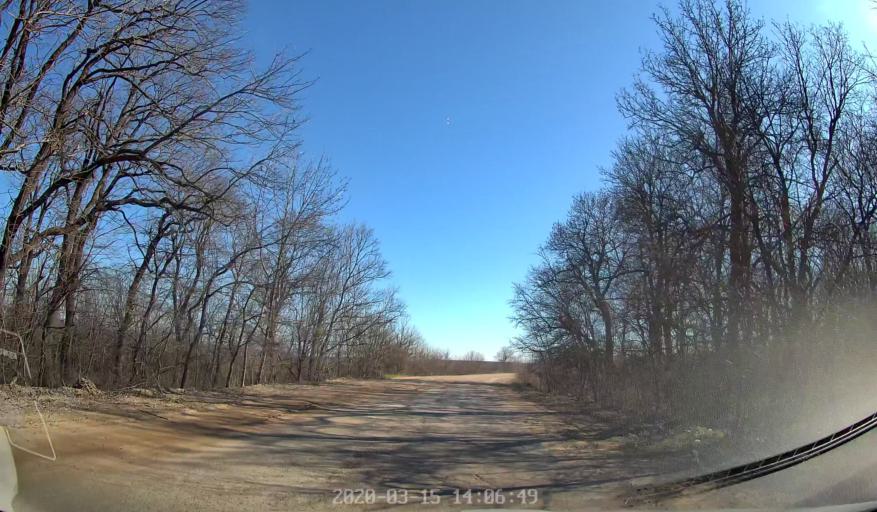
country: MD
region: Orhei
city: Orhei
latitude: 47.3023
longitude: 28.9488
